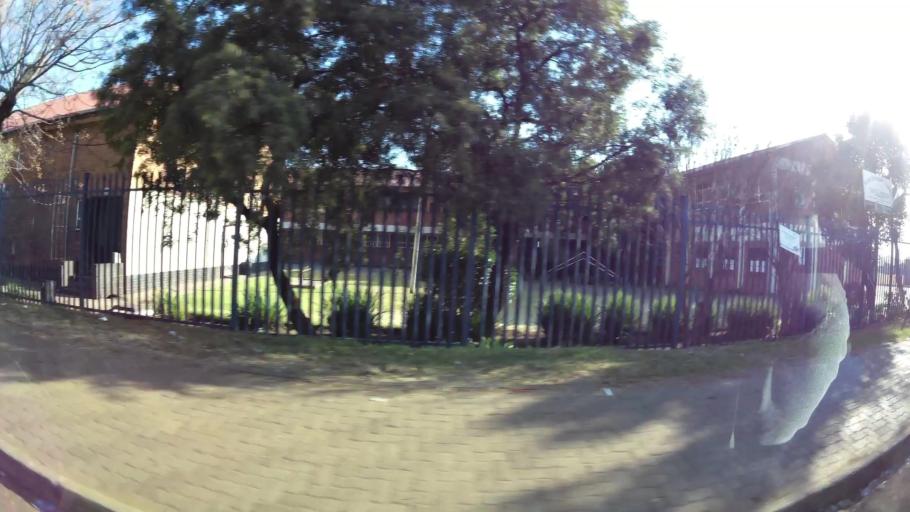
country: ZA
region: Gauteng
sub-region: Ekurhuleni Metropolitan Municipality
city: Boksburg
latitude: -26.1572
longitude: 28.2062
